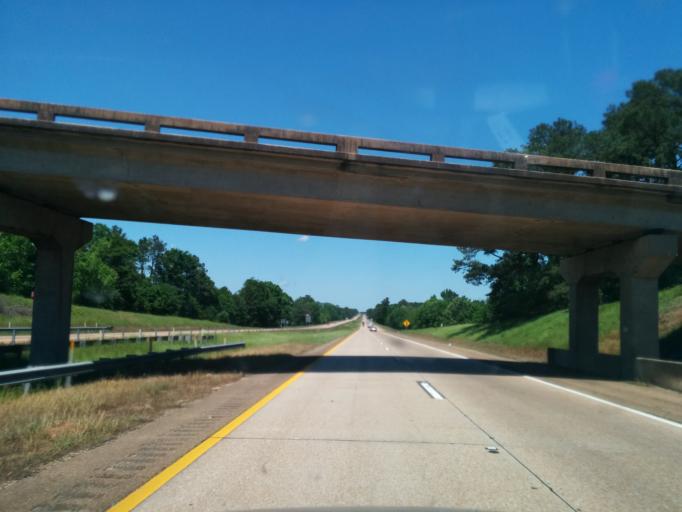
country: US
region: Mississippi
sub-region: Pike County
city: Magnolia
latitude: 31.1112
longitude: -90.4852
